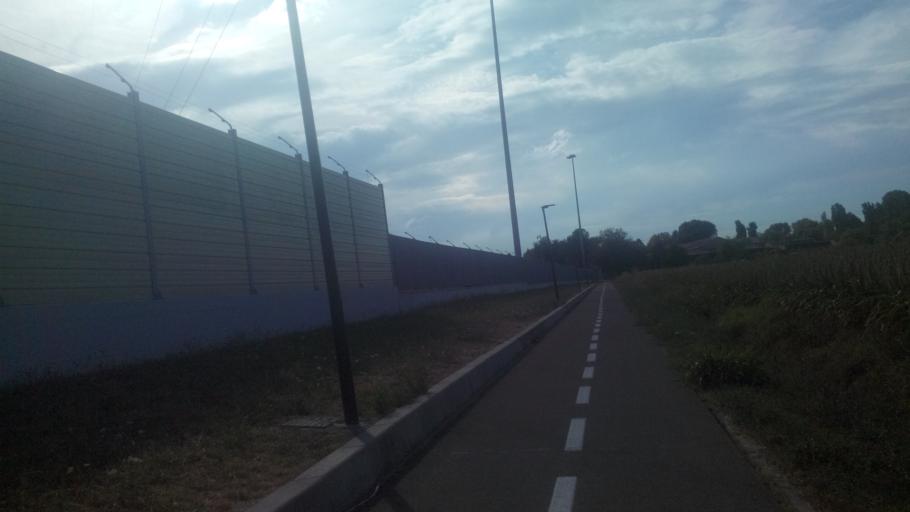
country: IT
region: Emilia-Romagna
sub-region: Provincia di Bologna
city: Bologna
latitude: 44.5234
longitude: 11.3573
